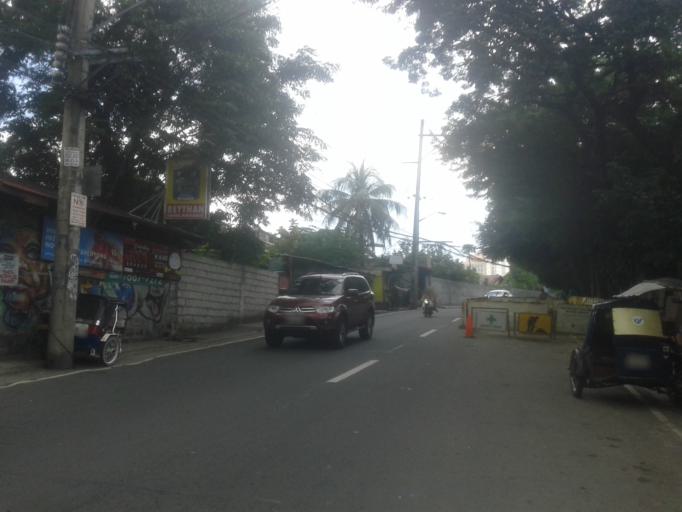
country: PH
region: Metro Manila
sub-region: Mandaluyong
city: Mandaluyong City
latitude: 14.5853
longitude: 121.0447
